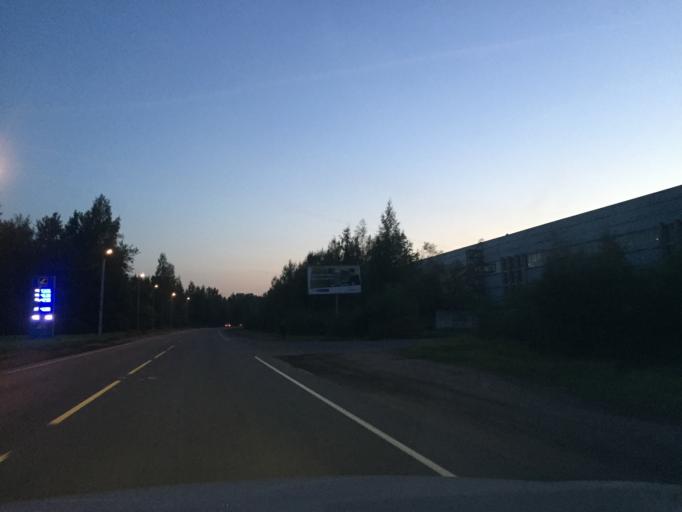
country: RU
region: Leningrad
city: Novoye Devyatkino
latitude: 60.0633
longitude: 30.4932
